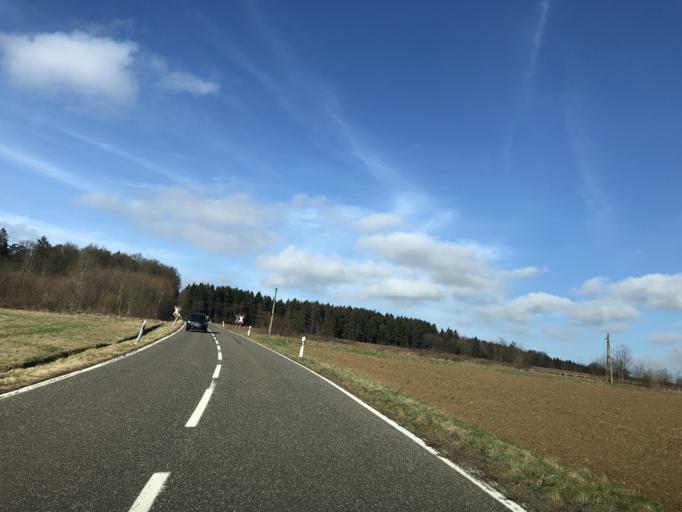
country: DE
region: Rheinland-Pfalz
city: Wahlenau
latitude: 49.9105
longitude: 7.2451
